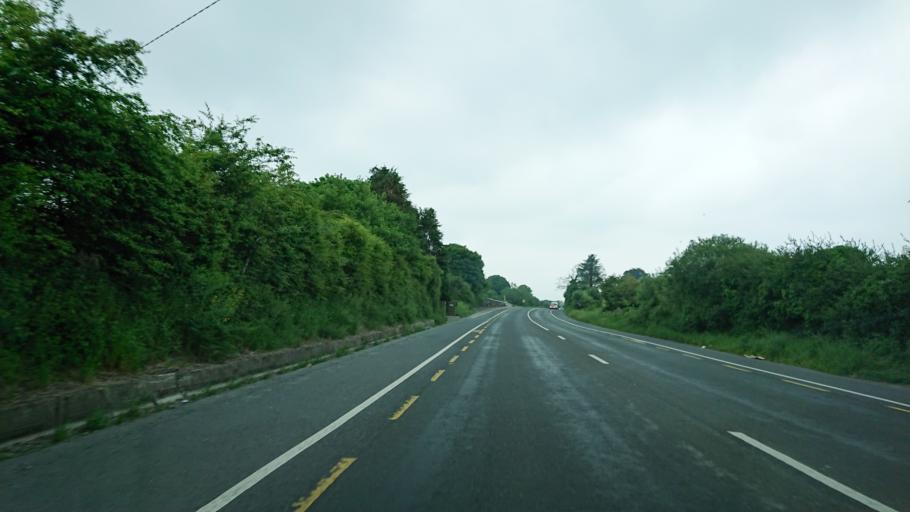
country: IE
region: Munster
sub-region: Waterford
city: Tra Mhor
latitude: 52.1910
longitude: -7.1266
